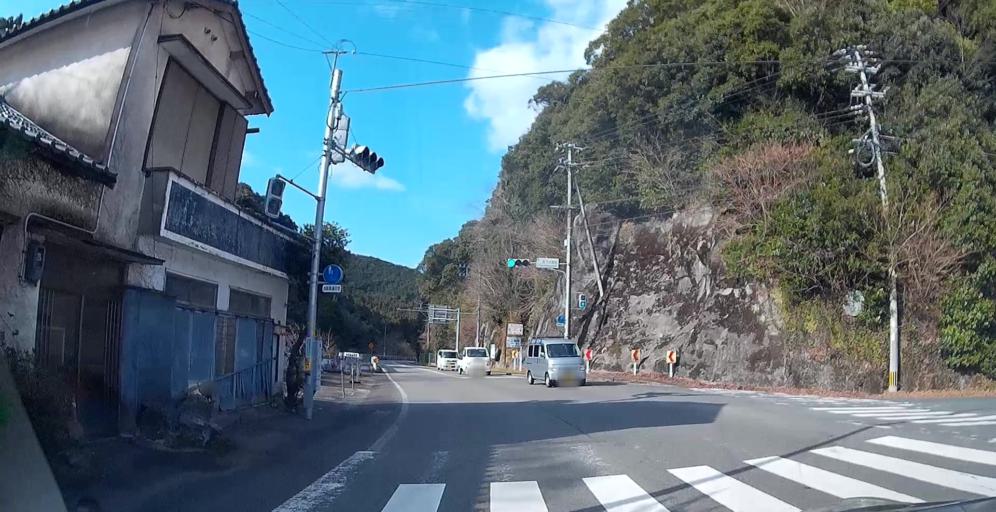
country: JP
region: Kumamoto
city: Yatsushiro
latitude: 32.4074
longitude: 130.5554
